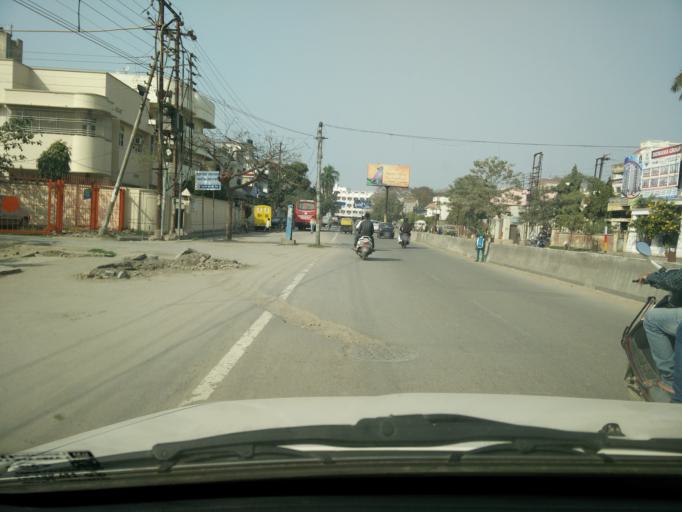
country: IN
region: Uttar Pradesh
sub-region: Varanasi
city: Varanasi
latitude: 25.2942
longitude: 83.0024
